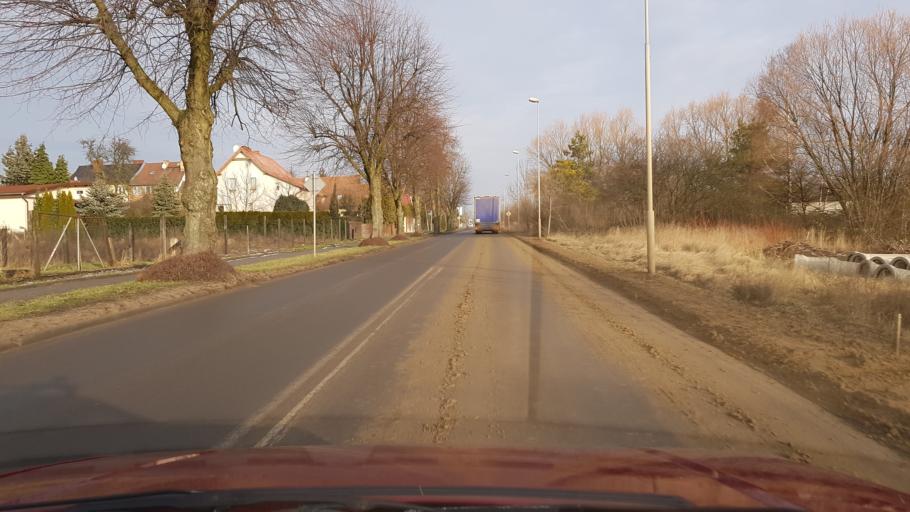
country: PL
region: West Pomeranian Voivodeship
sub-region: Powiat policki
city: Police
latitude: 53.4910
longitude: 14.5846
